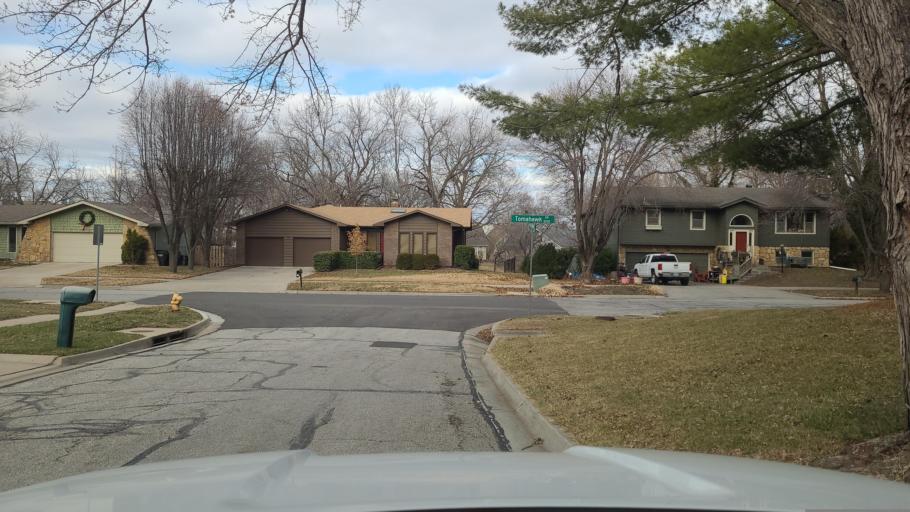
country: US
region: Kansas
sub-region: Douglas County
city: Lawrence
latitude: 38.9812
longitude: -95.2783
